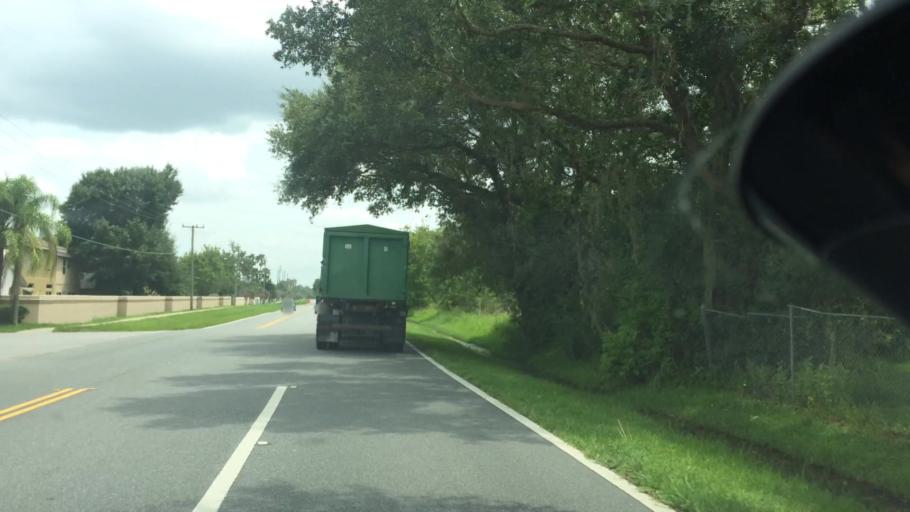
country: US
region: Florida
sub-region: Osceola County
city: Campbell
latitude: 28.2959
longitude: -81.4573
